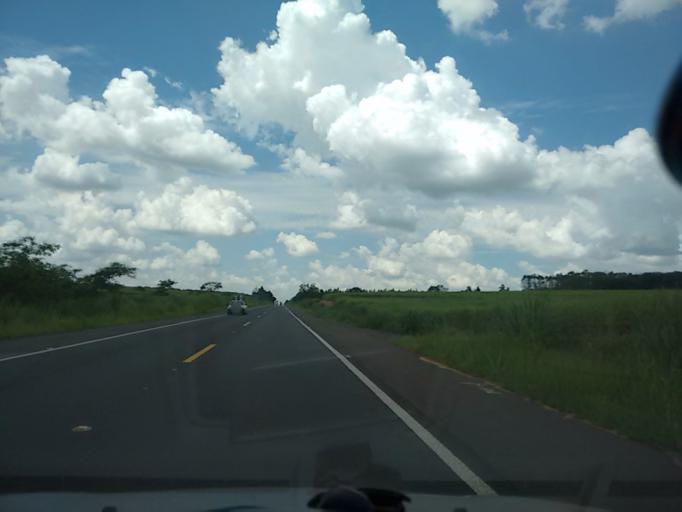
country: BR
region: Sao Paulo
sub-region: Osvaldo Cruz
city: Osvaldo Cruz
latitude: -21.8574
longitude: -50.8429
